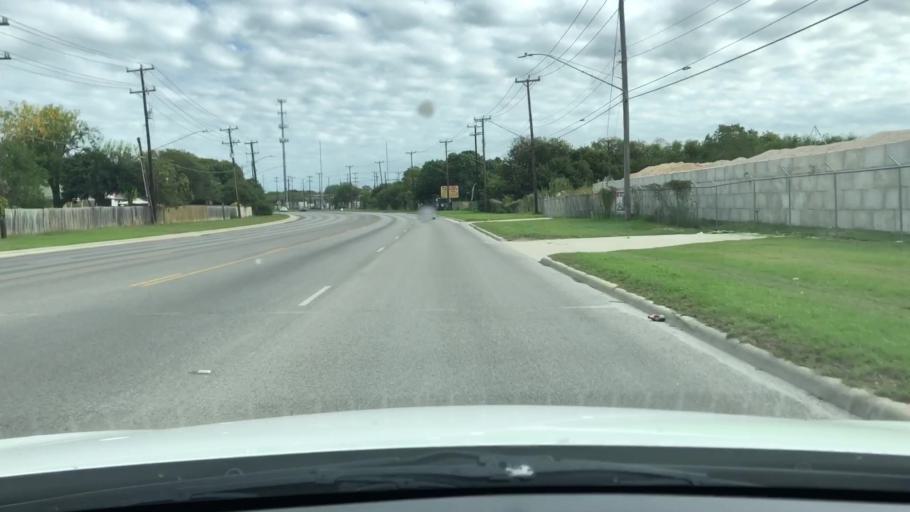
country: US
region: Texas
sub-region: Bexar County
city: Leon Valley
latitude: 29.4776
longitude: -98.6530
